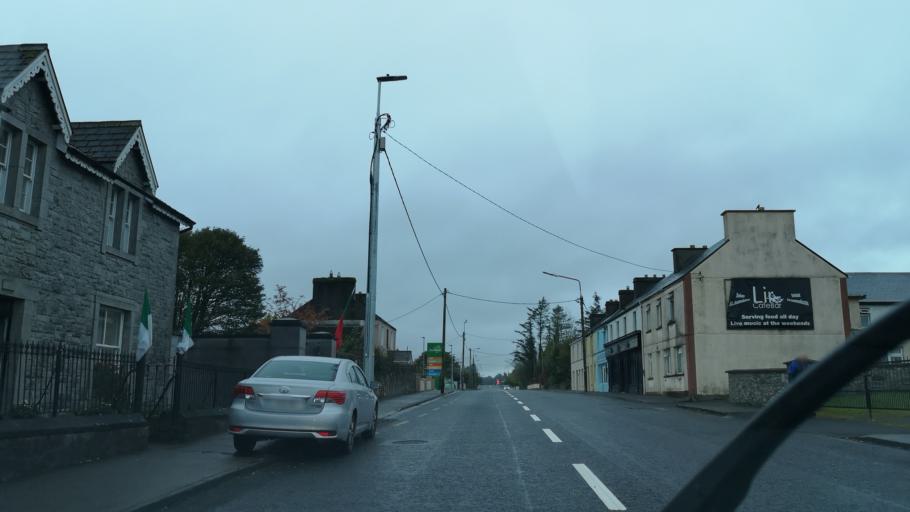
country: IE
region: Connaught
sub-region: Roscommon
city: Ballaghaderreen
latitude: 53.9028
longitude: -8.5820
